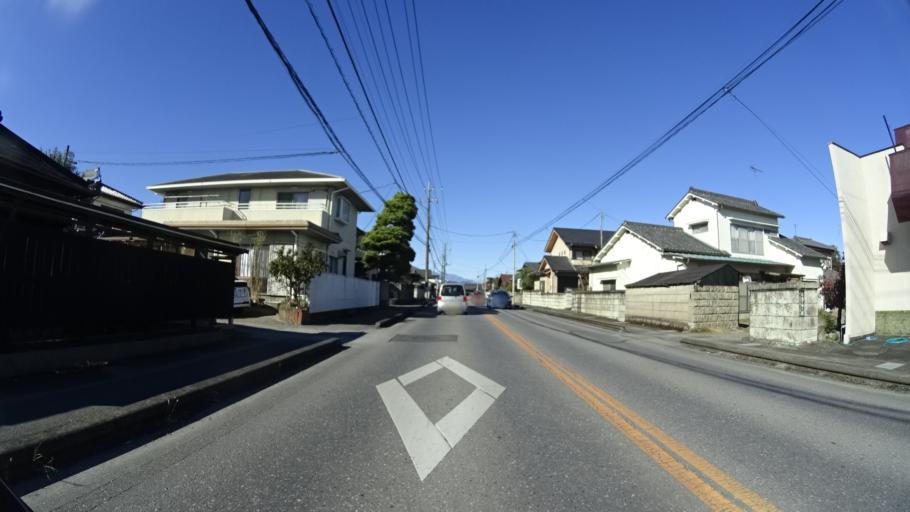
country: JP
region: Tochigi
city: Mibu
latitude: 36.4701
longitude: 139.7490
